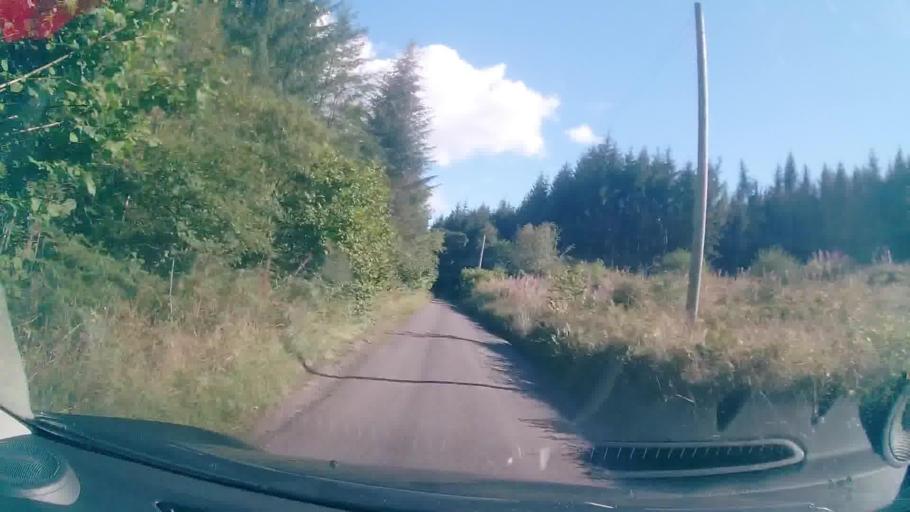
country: GB
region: Wales
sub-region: Merthyr Tydfil County Borough
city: Merthyr Tydfil
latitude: 51.8363
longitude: -3.3909
